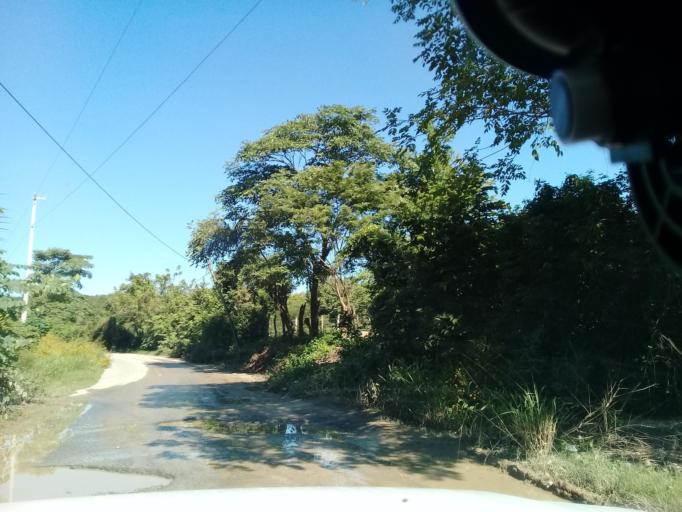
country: MX
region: Hidalgo
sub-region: Huejutla de Reyes
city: Huejutla de Reyes
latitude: 21.1639
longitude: -98.4188
